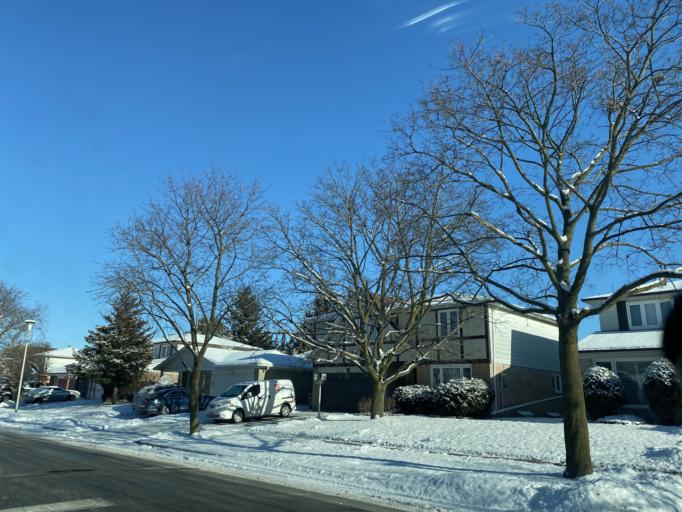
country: CA
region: Ontario
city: Scarborough
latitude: 43.7833
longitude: -79.3064
